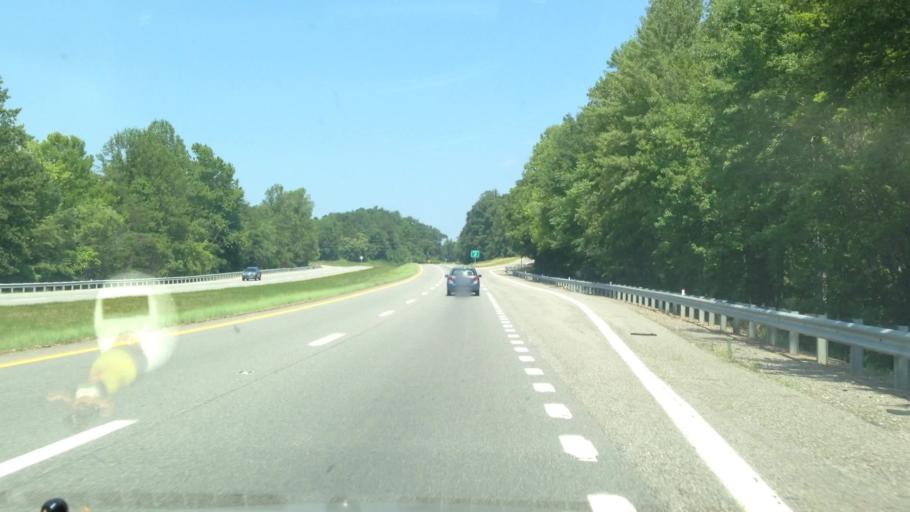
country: US
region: Virginia
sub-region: Henry County
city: Collinsville
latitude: 36.6919
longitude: -79.9474
